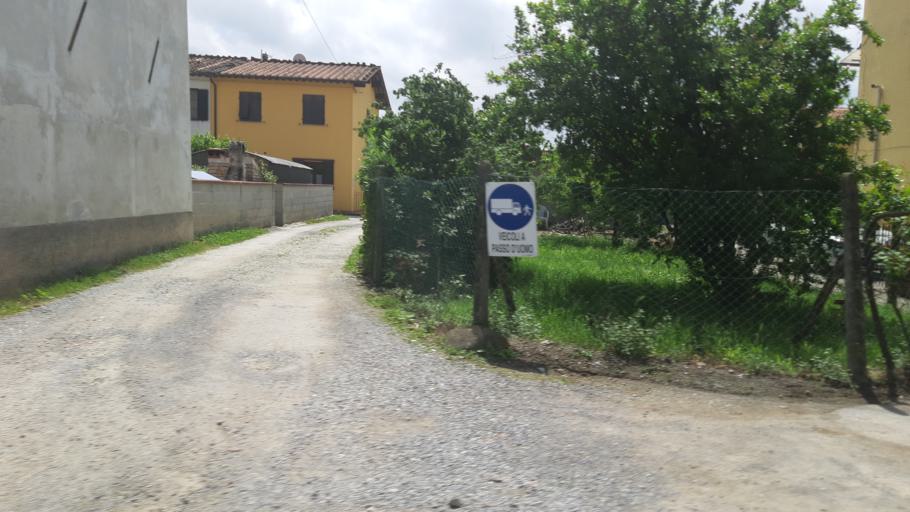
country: IT
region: Tuscany
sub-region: Provincia di Lucca
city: Capannori
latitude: 43.8684
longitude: 10.5633
